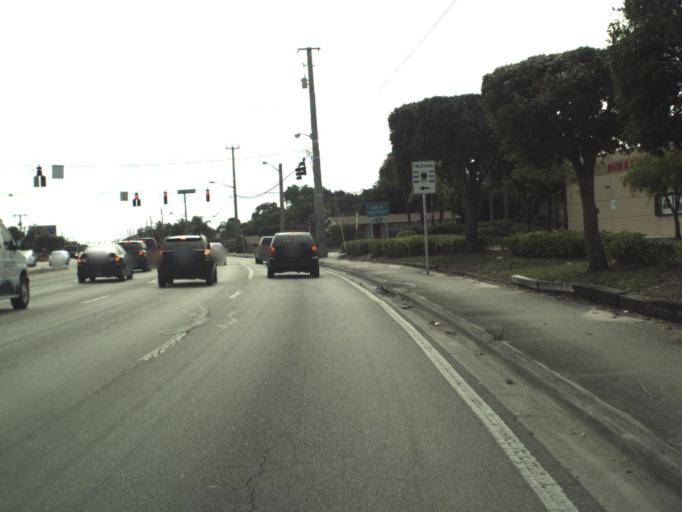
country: US
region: Florida
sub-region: Palm Beach County
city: Mangonia Park
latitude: 26.7533
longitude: -80.0788
